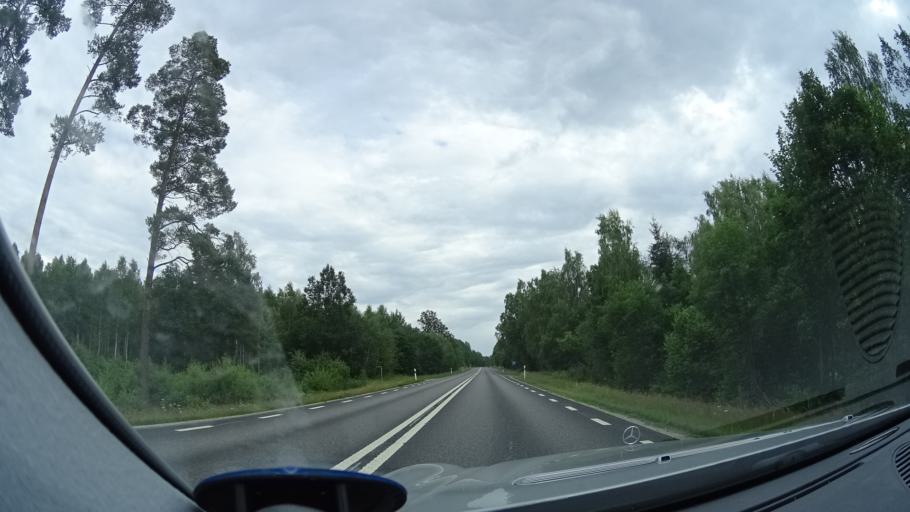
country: SE
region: Kronoberg
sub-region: Tingsryds Kommun
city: Tingsryd
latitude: 56.4939
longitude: 14.9977
